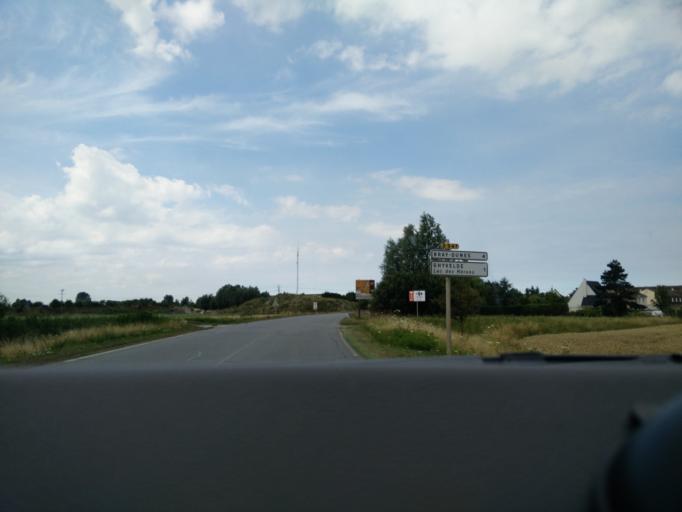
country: FR
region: Nord-Pas-de-Calais
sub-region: Departement du Nord
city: Ghyvelde
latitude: 51.0460
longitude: 2.5236
